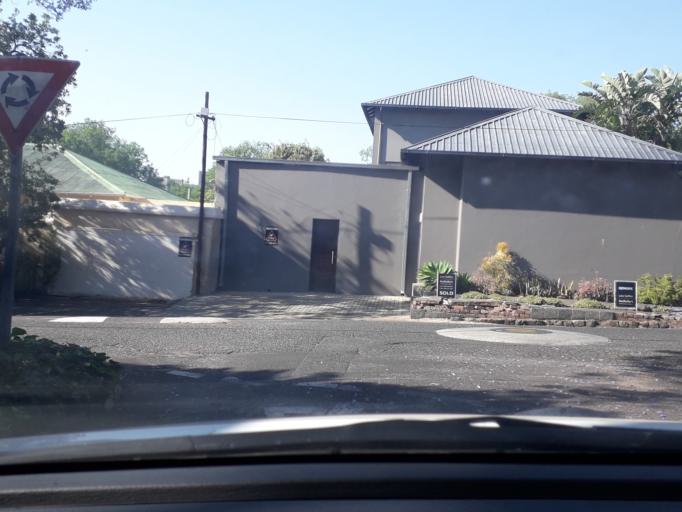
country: ZA
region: Gauteng
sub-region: City of Johannesburg Metropolitan Municipality
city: Johannesburg
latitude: -26.1783
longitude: 28.0125
